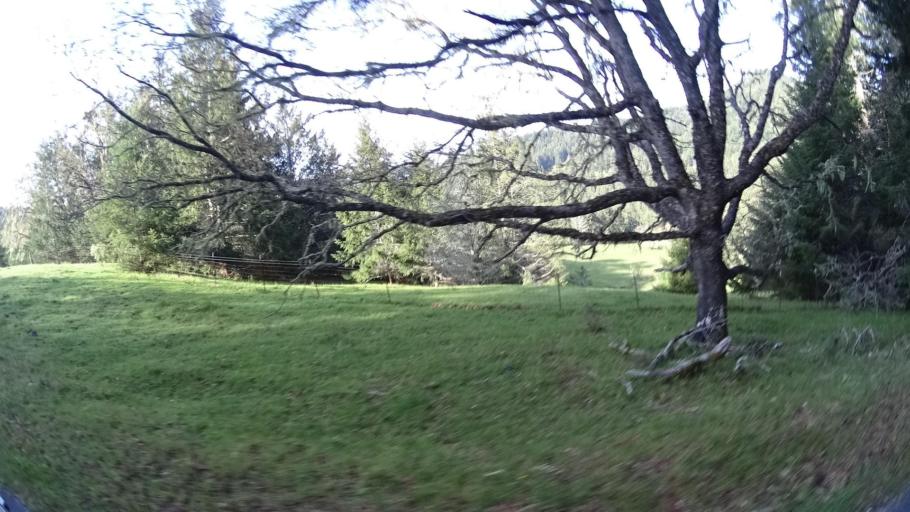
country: US
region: California
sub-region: Humboldt County
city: Bayside
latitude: 40.6922
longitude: -123.9414
